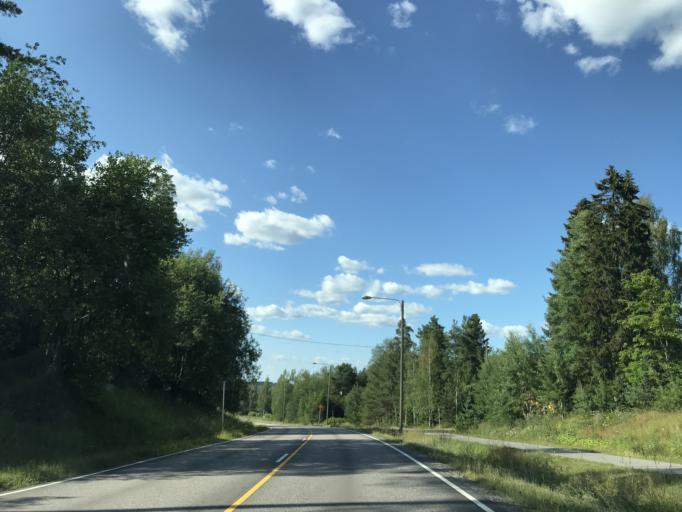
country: FI
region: Uusimaa
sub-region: Helsinki
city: Nurmijaervi
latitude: 60.4262
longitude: 24.8598
